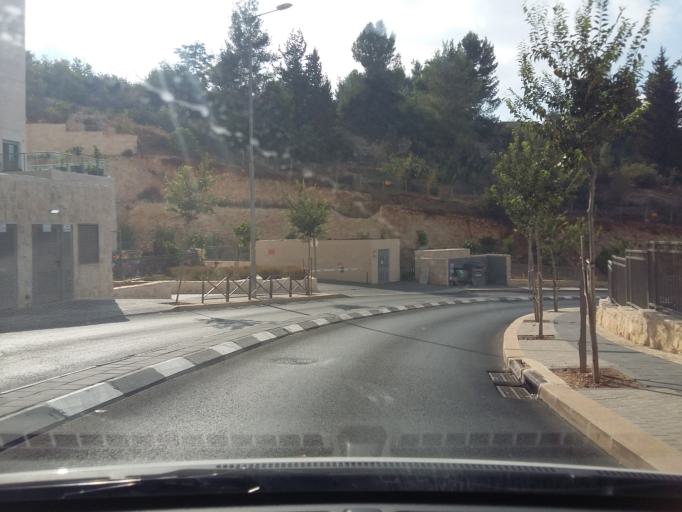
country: PS
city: Khallat Hamamah
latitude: 31.7605
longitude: 35.1676
